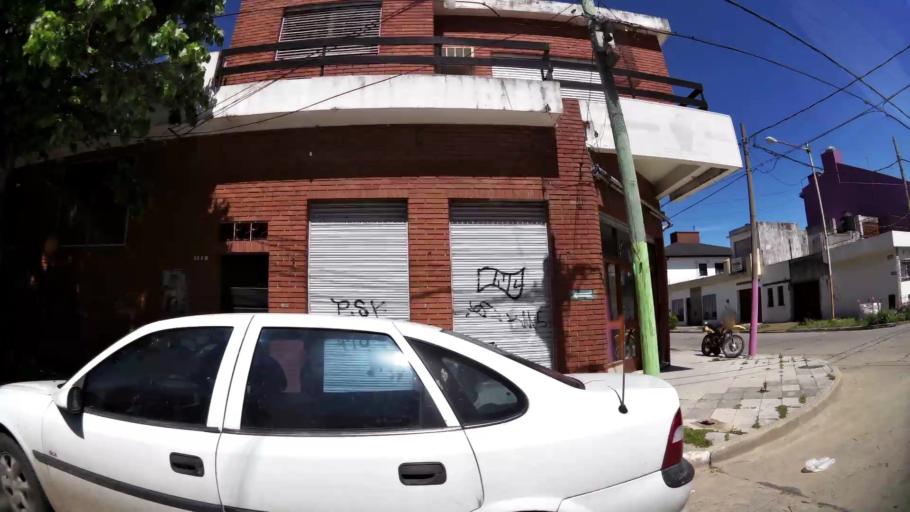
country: AR
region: Buenos Aires
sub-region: Partido de Quilmes
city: Quilmes
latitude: -34.7153
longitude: -58.2693
